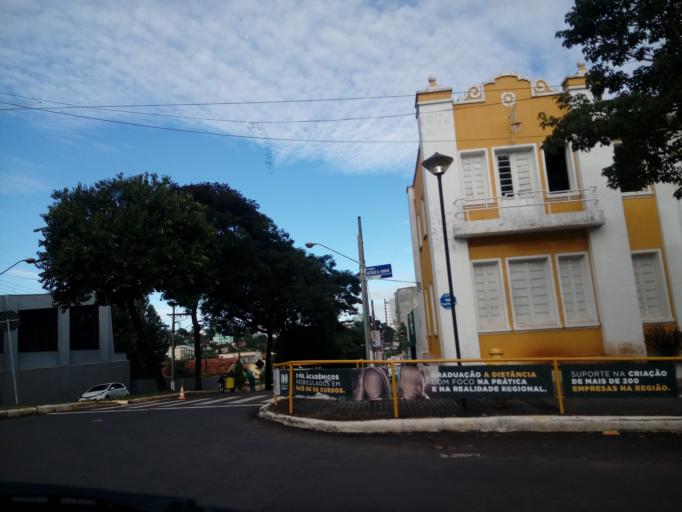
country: BR
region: Santa Catarina
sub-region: Chapeco
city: Chapeco
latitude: -27.1047
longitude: -52.6143
